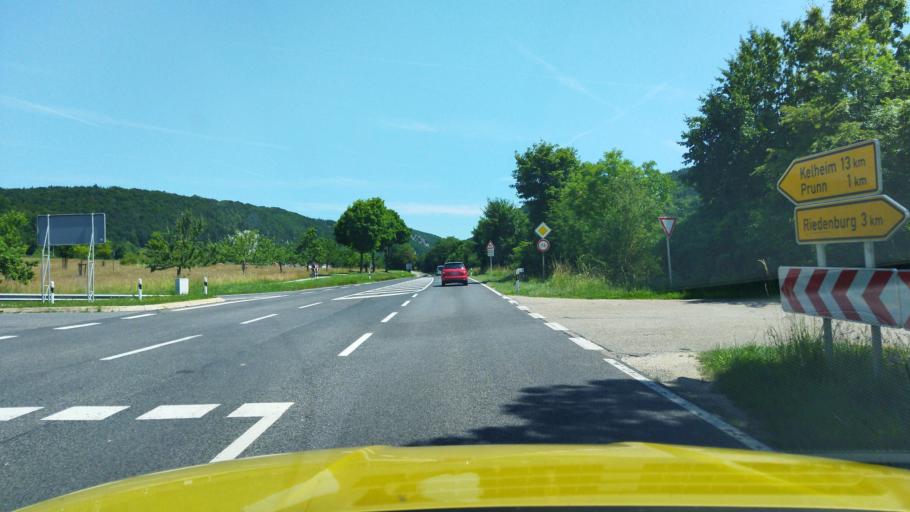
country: DE
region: Bavaria
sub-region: Lower Bavaria
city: Riedenburg
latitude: 48.9565
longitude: 11.7154
